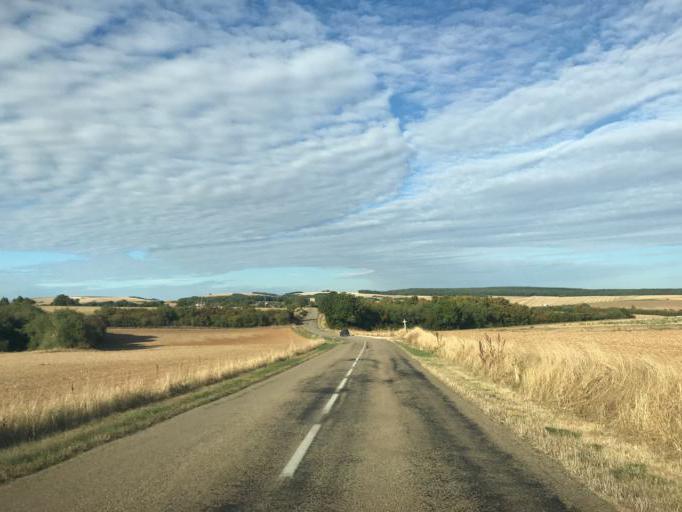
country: FR
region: Bourgogne
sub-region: Departement de l'Yonne
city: Fontenailles
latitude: 47.6055
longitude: 3.4869
